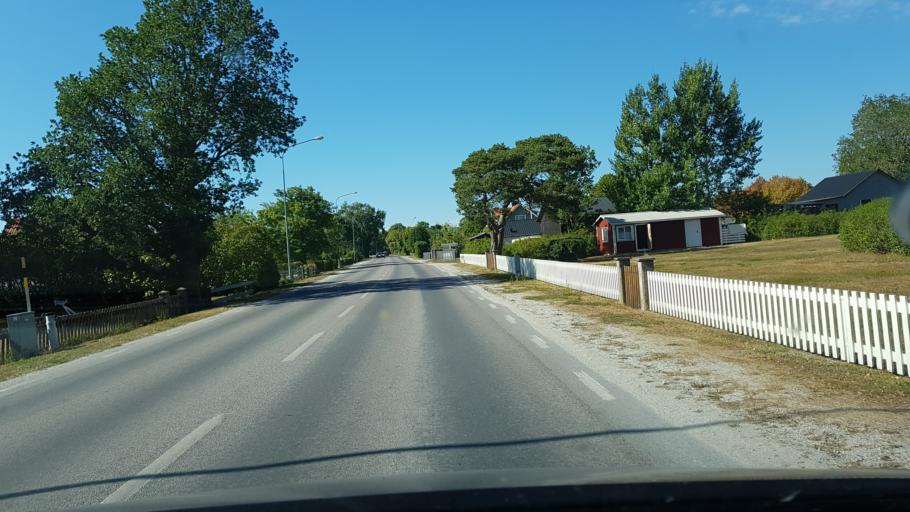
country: SE
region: Gotland
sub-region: Gotland
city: Klintehamn
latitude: 57.4343
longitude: 18.1463
